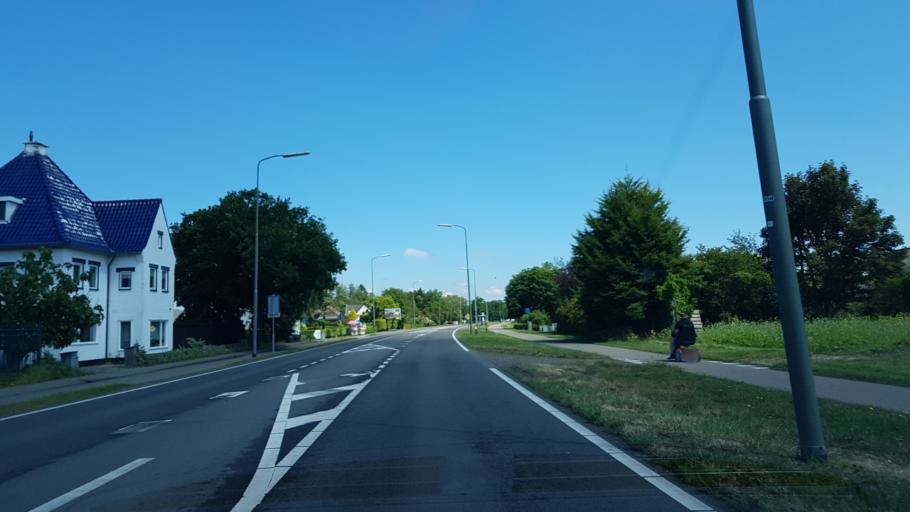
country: NL
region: South Holland
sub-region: Gemeente Voorschoten
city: Voorschoten
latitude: 52.1020
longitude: 4.4180
